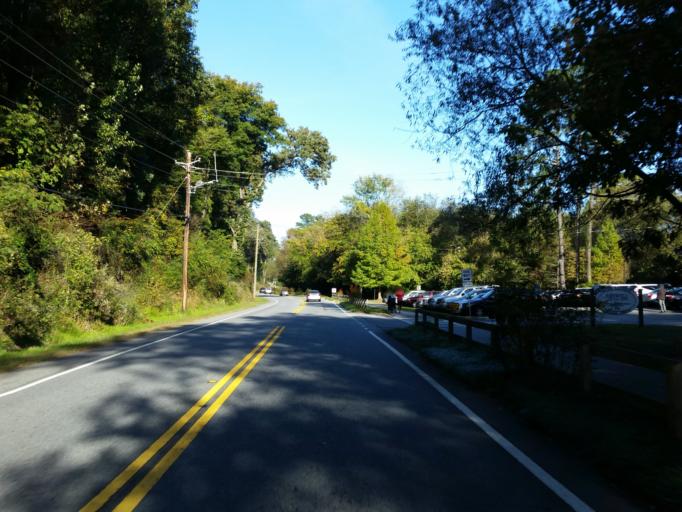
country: US
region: Georgia
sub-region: Fulton County
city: Roswell
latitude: 34.0034
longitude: -84.3575
